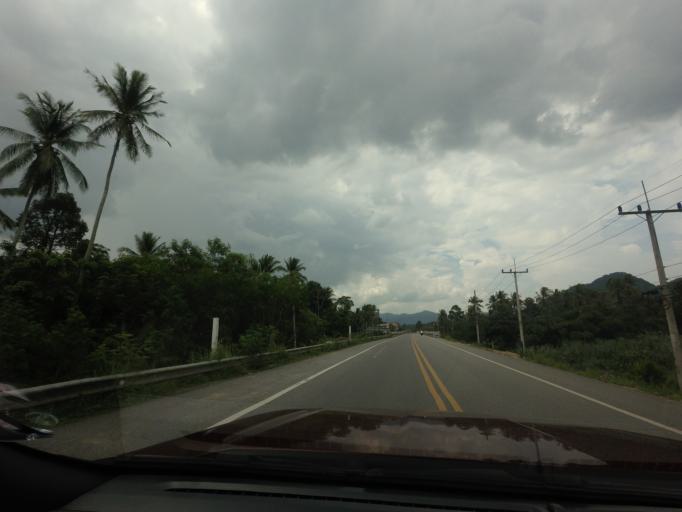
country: TH
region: Yala
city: Ban Nang Sata
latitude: 6.3036
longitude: 101.3016
